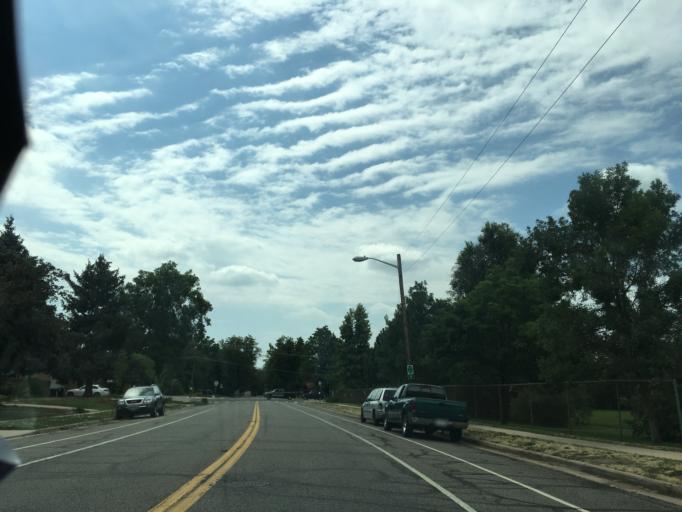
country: US
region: Colorado
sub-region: Arapahoe County
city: Sheridan
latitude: 39.6602
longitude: -105.0440
